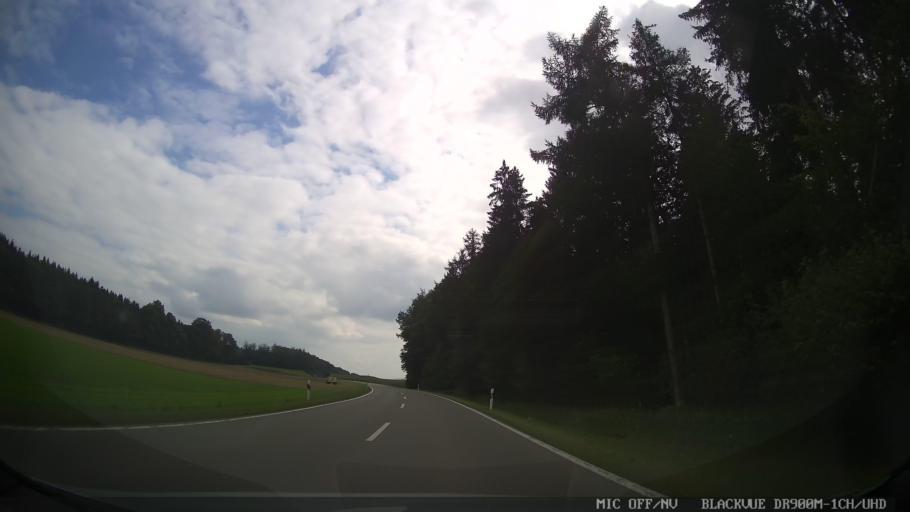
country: DE
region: Baden-Wuerttemberg
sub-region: Freiburg Region
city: Orsingen-Nenzingen
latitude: 47.8943
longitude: 8.9690
